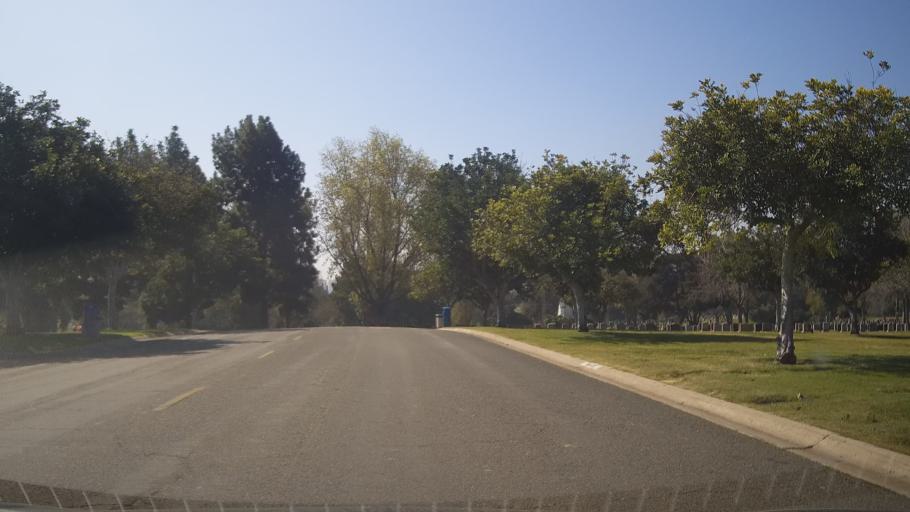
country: US
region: California
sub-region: San Diego County
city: National City
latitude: 32.7094
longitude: -117.1128
